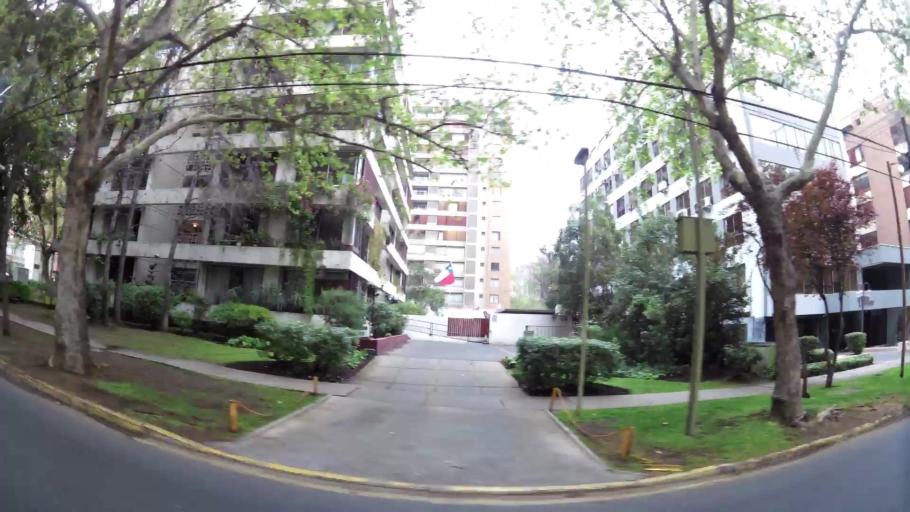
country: CL
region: Santiago Metropolitan
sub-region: Provincia de Santiago
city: Villa Presidente Frei, Nunoa, Santiago, Chile
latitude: -33.4182
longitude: -70.5974
